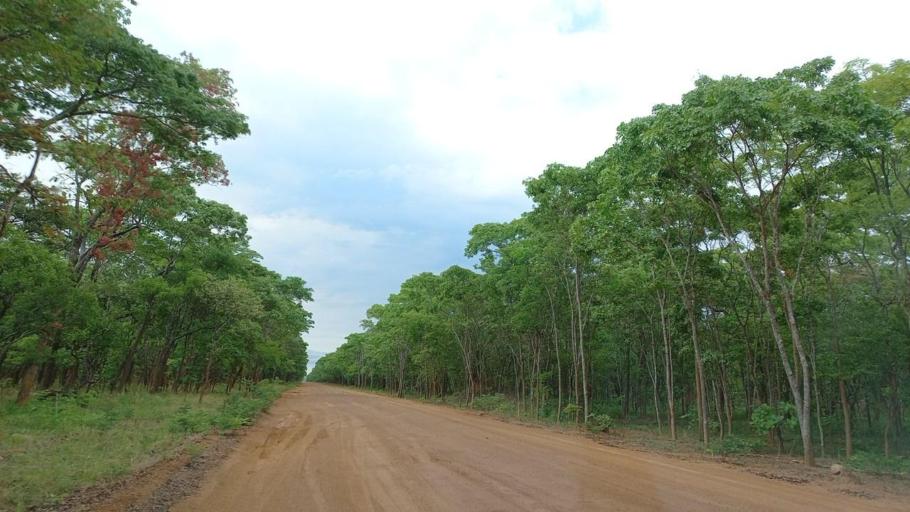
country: ZM
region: North-Western
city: Kalengwa
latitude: -13.3573
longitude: 25.0765
